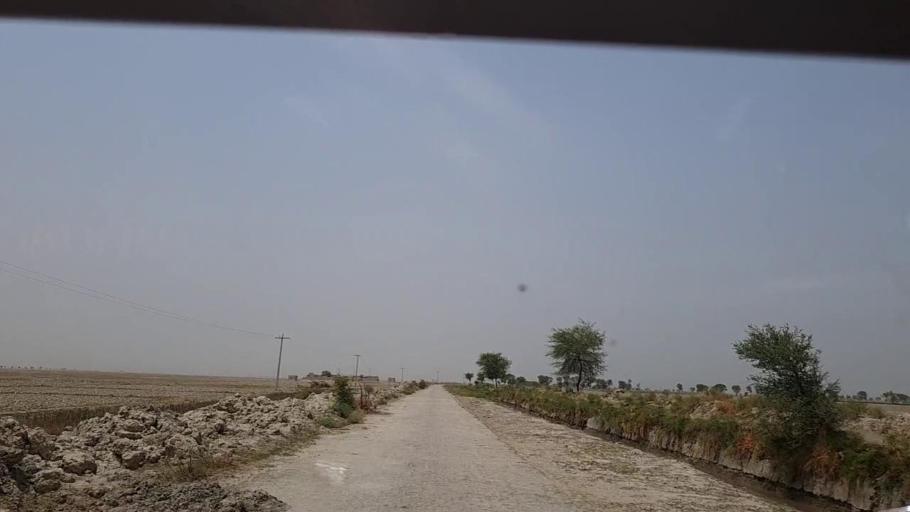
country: PK
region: Sindh
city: Khairpur Nathan Shah
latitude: 27.0365
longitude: 67.6190
